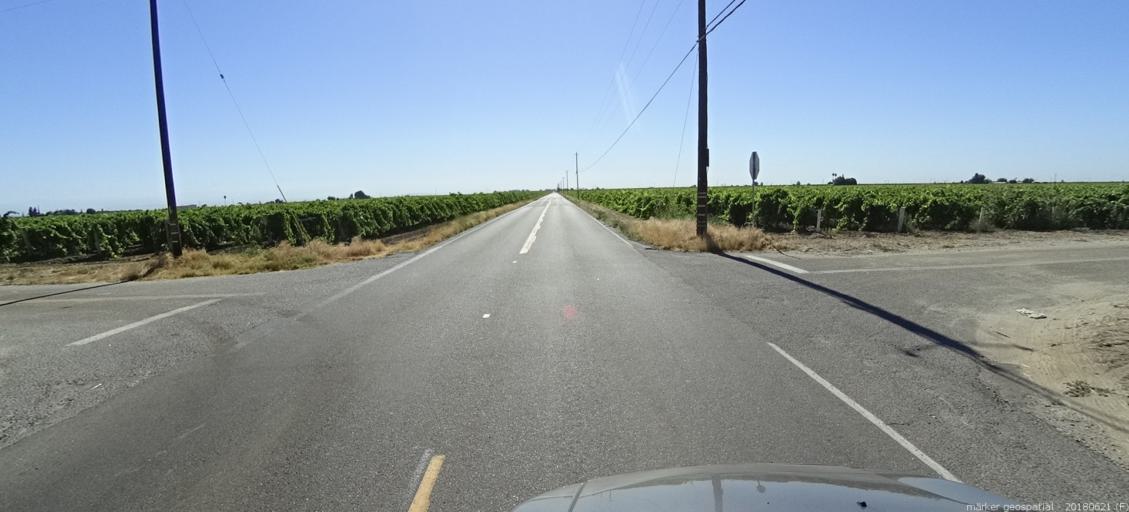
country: US
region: California
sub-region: Fresno County
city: Biola
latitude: 36.8513
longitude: -120.0287
